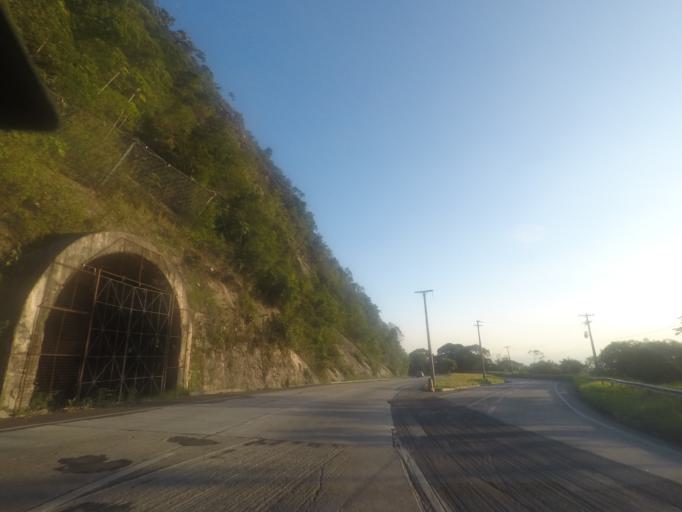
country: BR
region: Rio de Janeiro
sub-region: Petropolis
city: Petropolis
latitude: -22.5326
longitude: -43.2335
